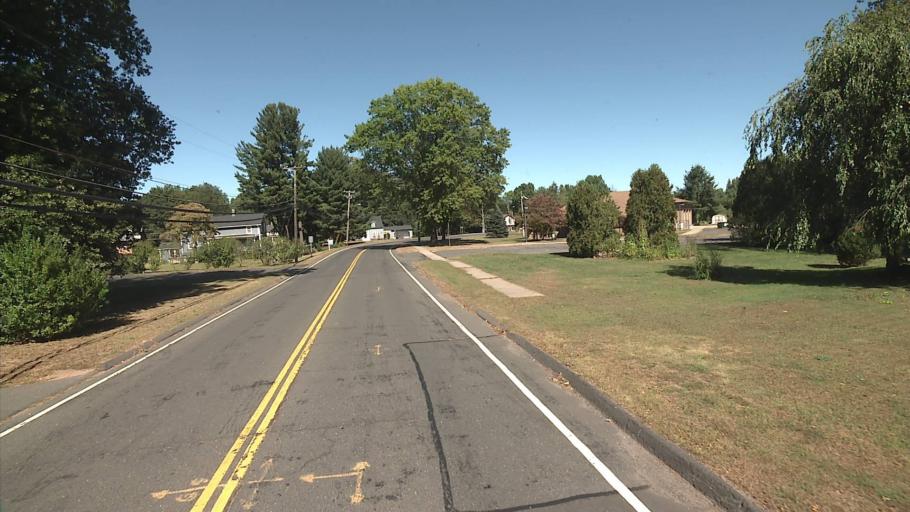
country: US
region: Connecticut
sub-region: New Haven County
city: Cheshire Village
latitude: 41.5689
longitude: -72.8990
